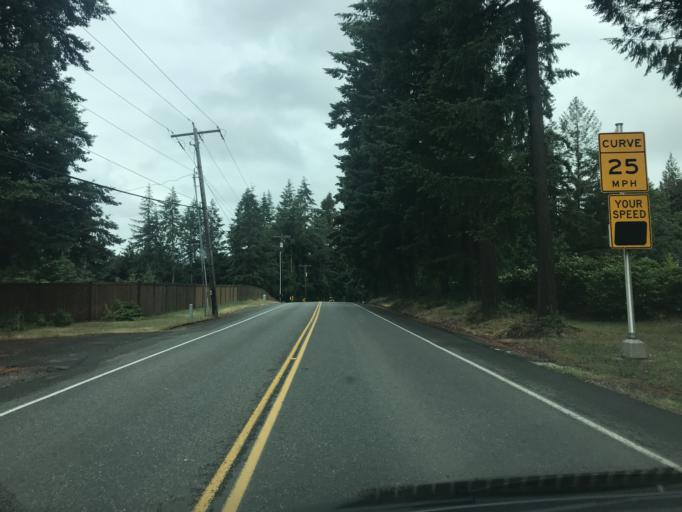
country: US
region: Washington
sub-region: King County
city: Lake Morton-Berrydale
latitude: 47.3420
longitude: -122.0969
